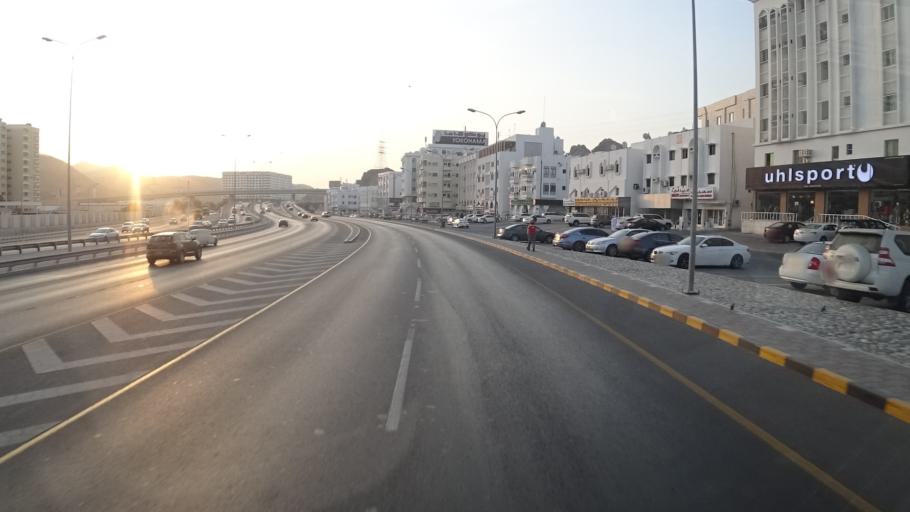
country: OM
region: Muhafazat Masqat
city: Muscat
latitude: 23.5908
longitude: 58.5312
